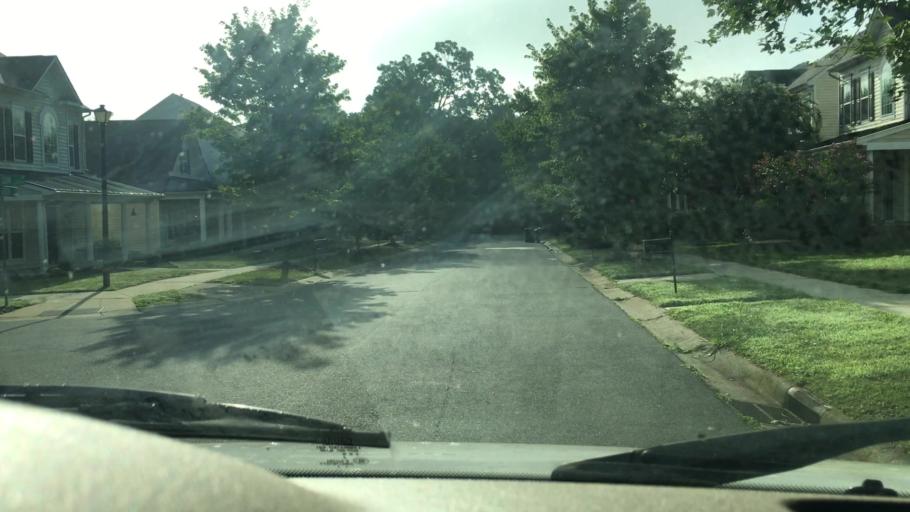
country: US
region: North Carolina
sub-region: Mecklenburg County
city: Huntersville
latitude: 35.3853
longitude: -80.9183
